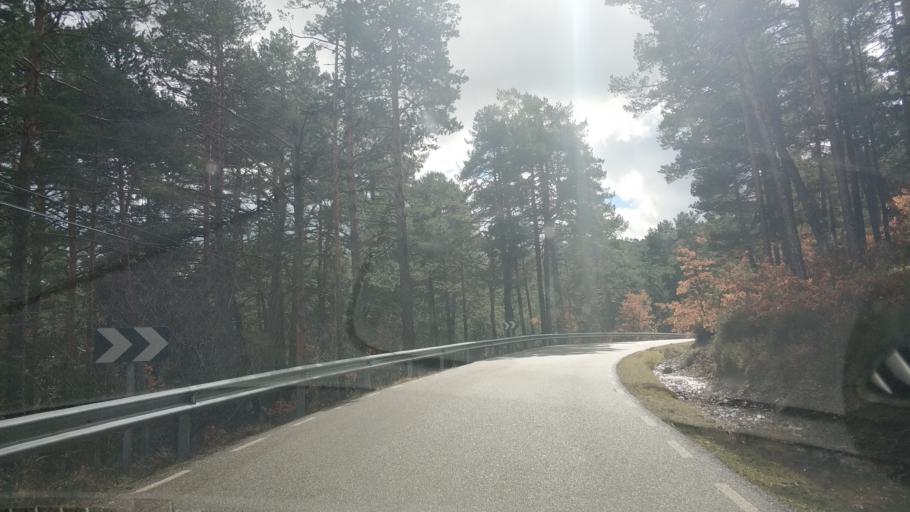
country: ES
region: Castille and Leon
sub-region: Provincia de Burgos
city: Quintanar de la Sierra
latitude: 42.0083
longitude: -3.0199
